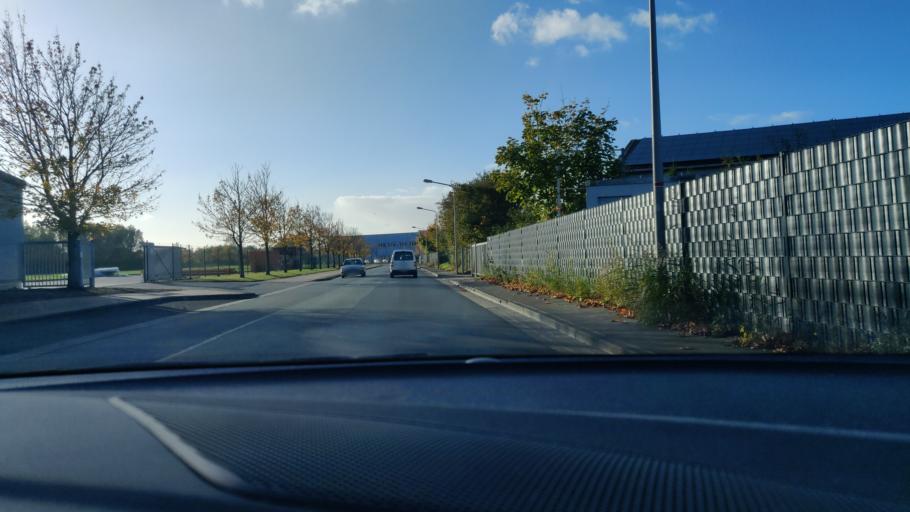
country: DE
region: Lower Saxony
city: Cuxhaven
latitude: 53.8473
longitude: 8.7044
